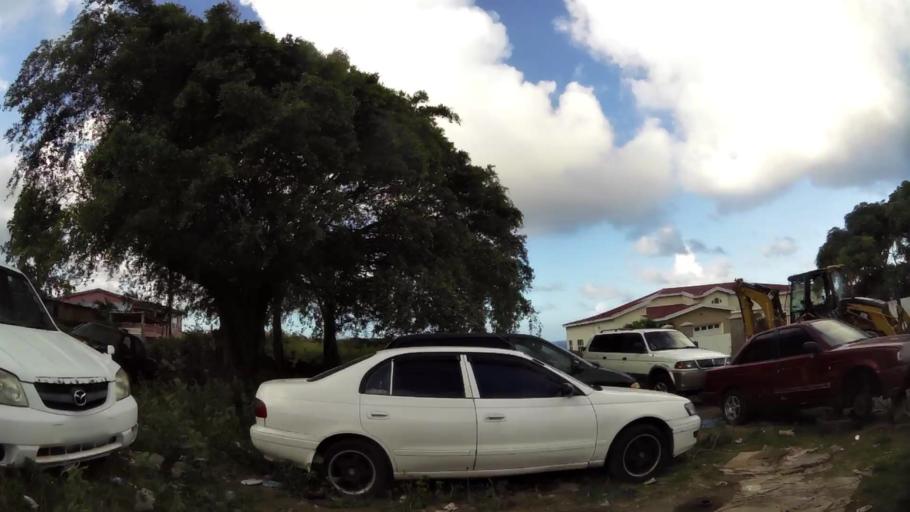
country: KN
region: Saint Mary Cayon
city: Cayon
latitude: 17.3509
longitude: -62.7268
